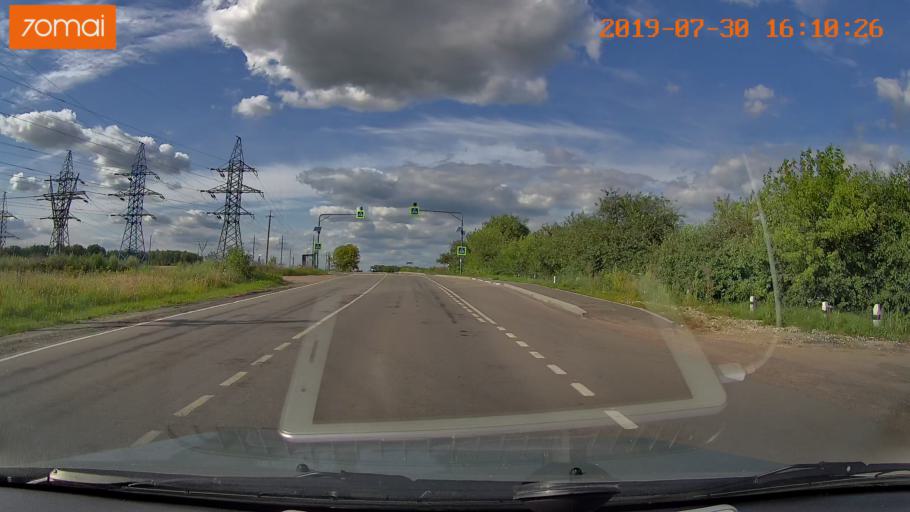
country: RU
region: Moskovskaya
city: Peski
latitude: 55.2626
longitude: 38.7156
